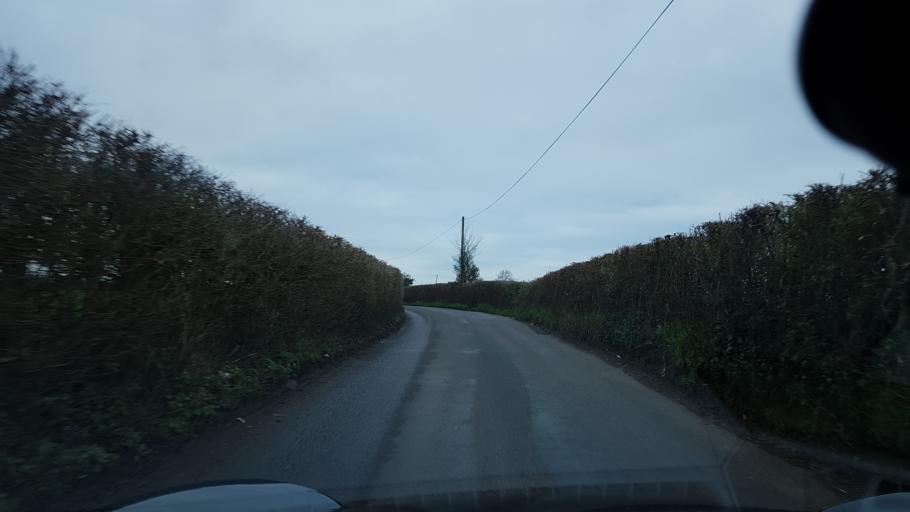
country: GB
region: England
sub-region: Somerset
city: Creech Saint Michael
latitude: 51.0062
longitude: -3.0483
